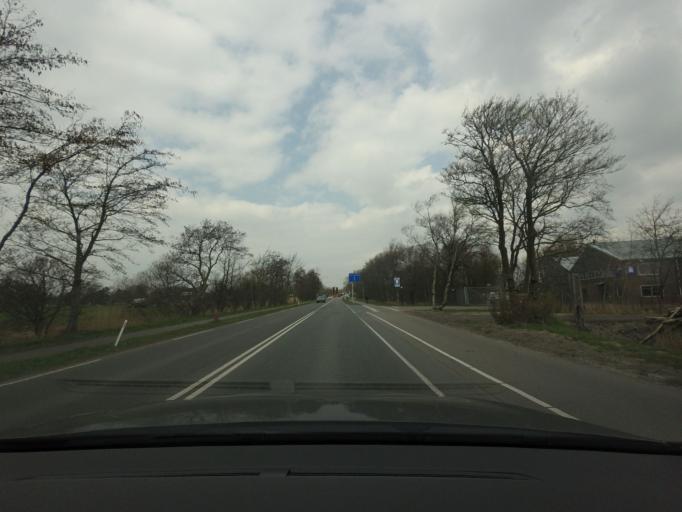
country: NL
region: North Holland
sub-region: Gemeente Alkmaar
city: Alkmaar
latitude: 52.6588
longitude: 4.7171
